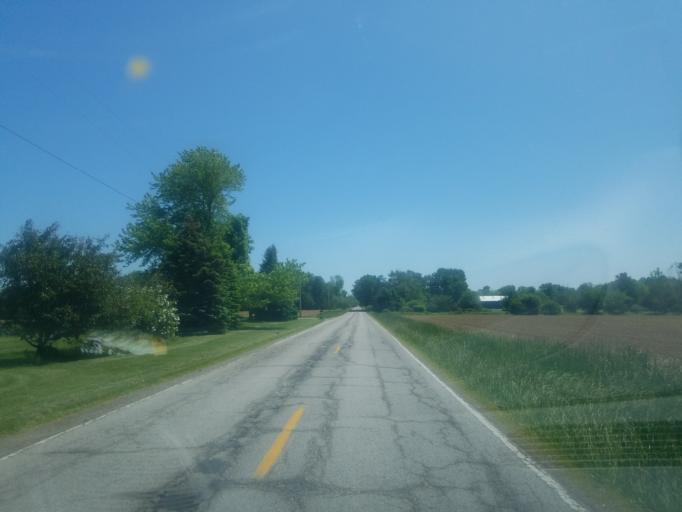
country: US
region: Ohio
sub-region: Huron County
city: Wakeman
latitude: 41.1967
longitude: -82.3755
